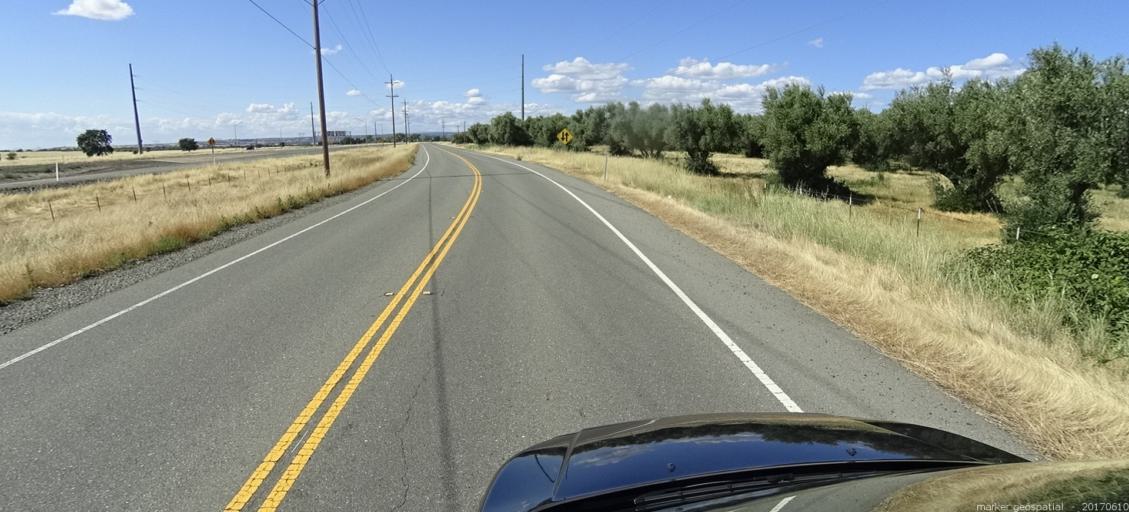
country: US
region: California
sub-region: Butte County
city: Thermalito
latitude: 39.5856
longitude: -121.6186
